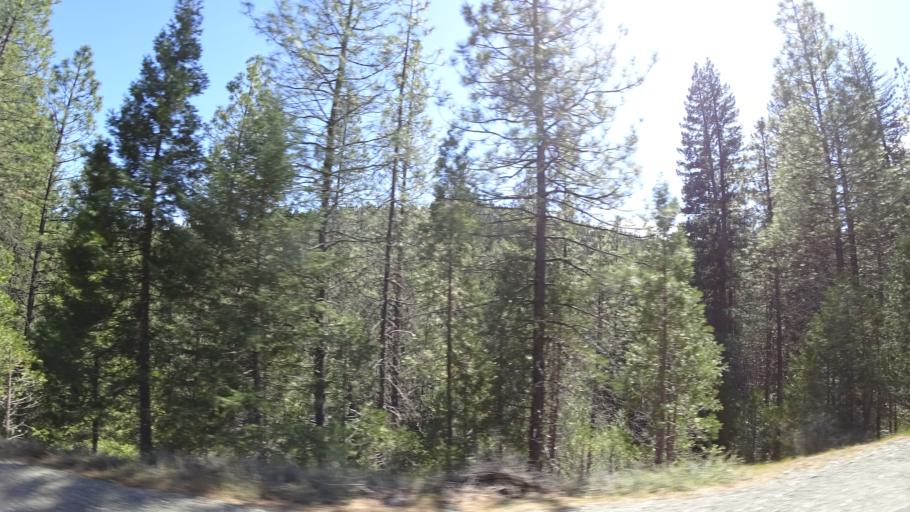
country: US
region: California
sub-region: Trinity County
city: Lewiston
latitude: 40.9048
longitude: -122.7809
